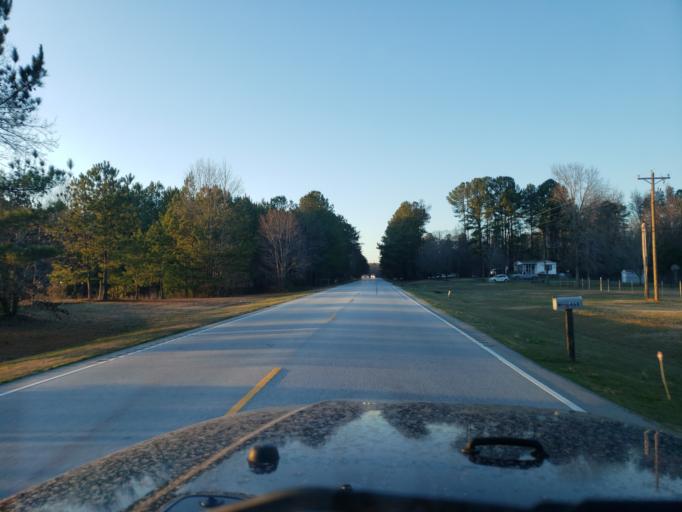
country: US
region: North Carolina
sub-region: Cleveland County
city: Kings Mountain
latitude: 35.1520
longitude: -81.3220
